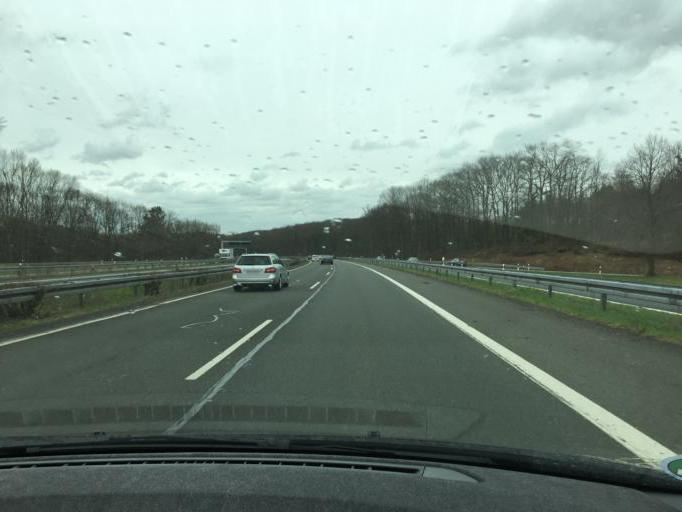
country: DE
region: North Rhine-Westphalia
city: Herdecke
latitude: 51.4446
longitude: 7.4859
